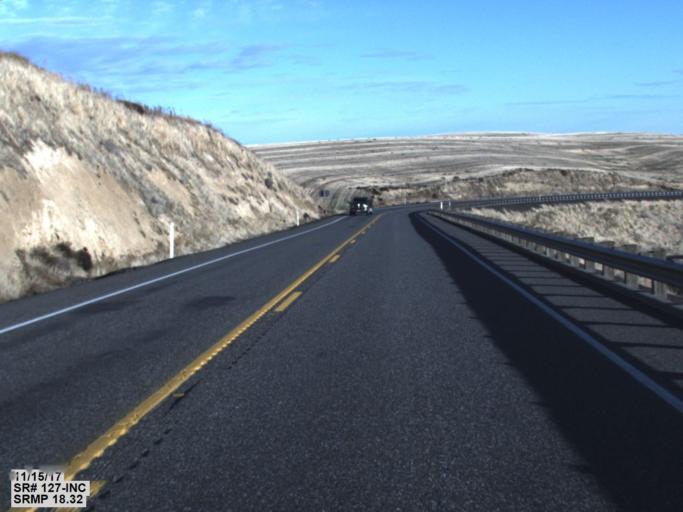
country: US
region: Washington
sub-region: Garfield County
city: Pomeroy
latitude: 46.7226
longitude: -117.7680
